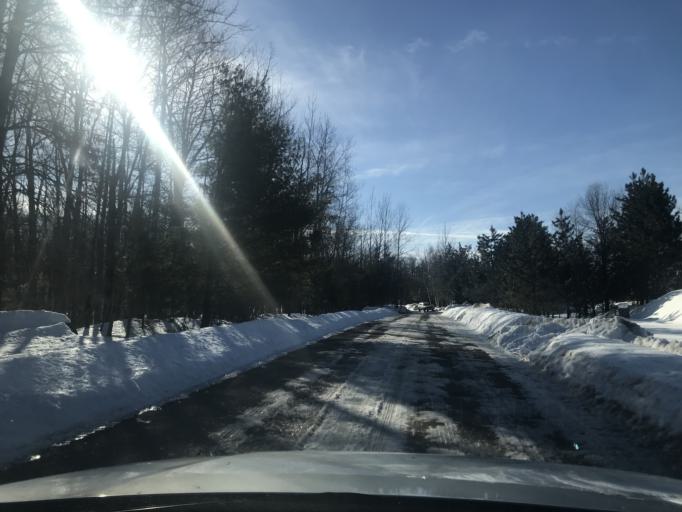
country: US
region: Wisconsin
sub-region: Marinette County
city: Niagara
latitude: 45.4235
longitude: -88.0209
